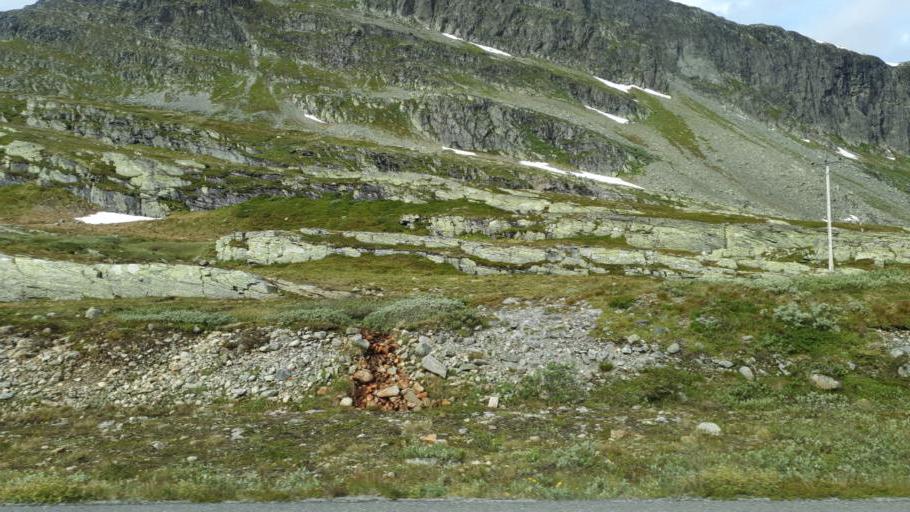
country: NO
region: Oppland
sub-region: Vestre Slidre
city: Slidre
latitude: 61.2944
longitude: 8.8138
